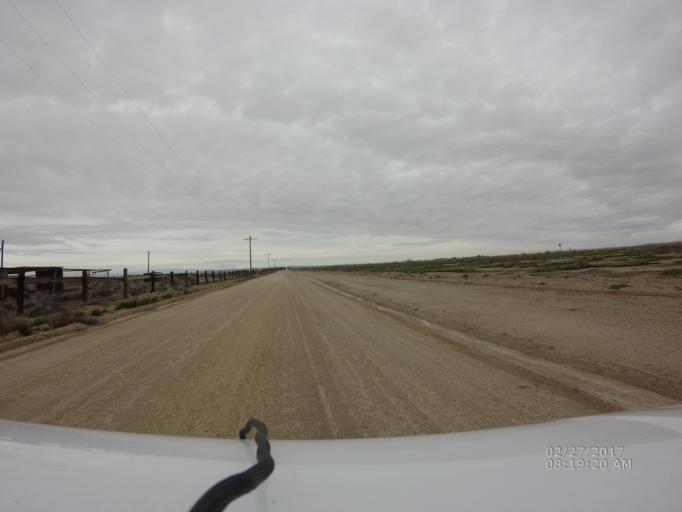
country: US
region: California
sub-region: Los Angeles County
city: Lancaster
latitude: 34.7205
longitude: -118.0144
